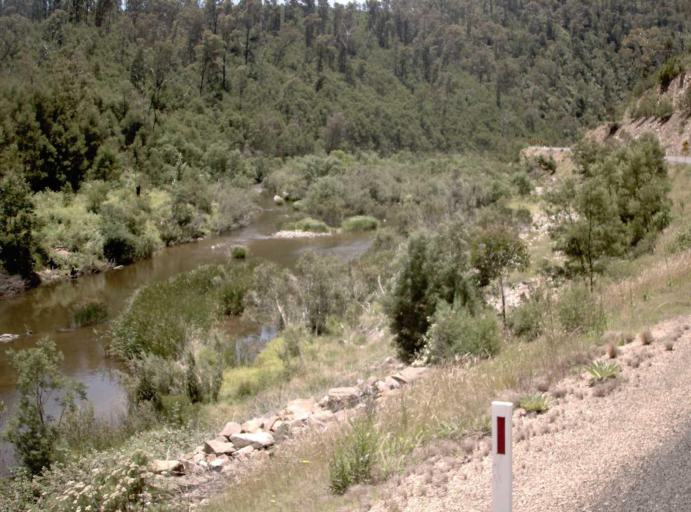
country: AU
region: Victoria
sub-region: East Gippsland
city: Bairnsdale
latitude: -37.5293
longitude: 147.8453
